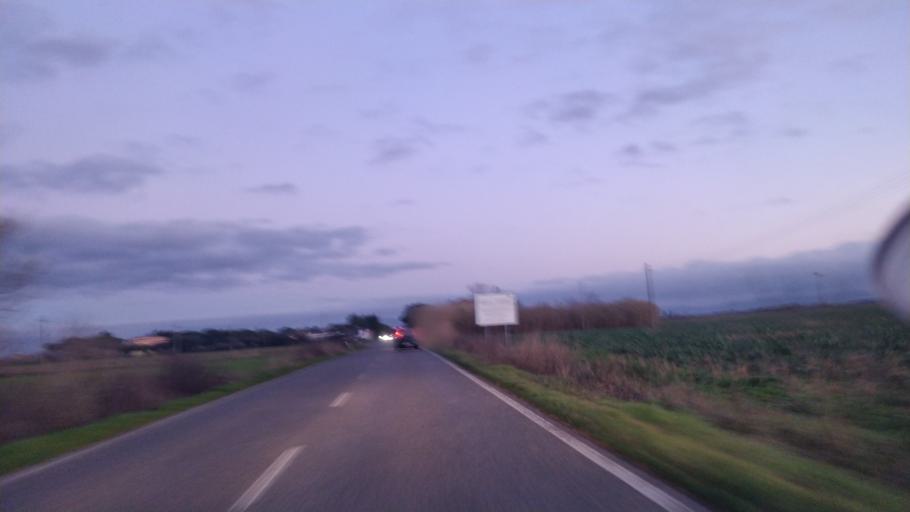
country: IT
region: Tuscany
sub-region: Provincia di Livorno
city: Vada
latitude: 43.3450
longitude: 10.4707
